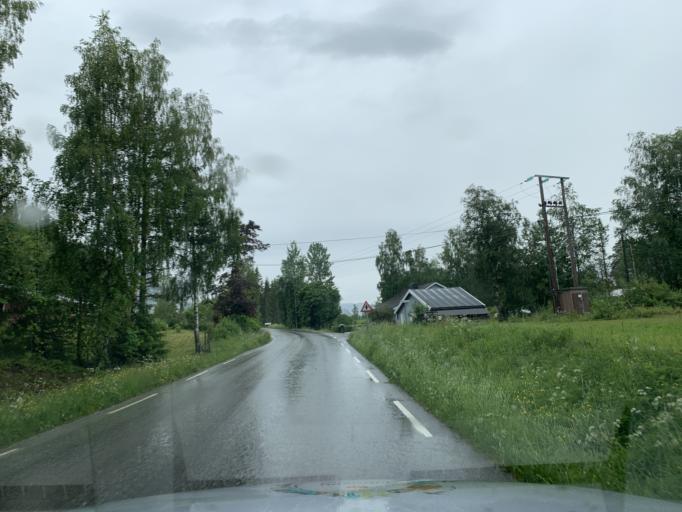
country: NO
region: Oppland
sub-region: Ringebu
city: Ringebu
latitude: 61.4472
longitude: 10.1797
